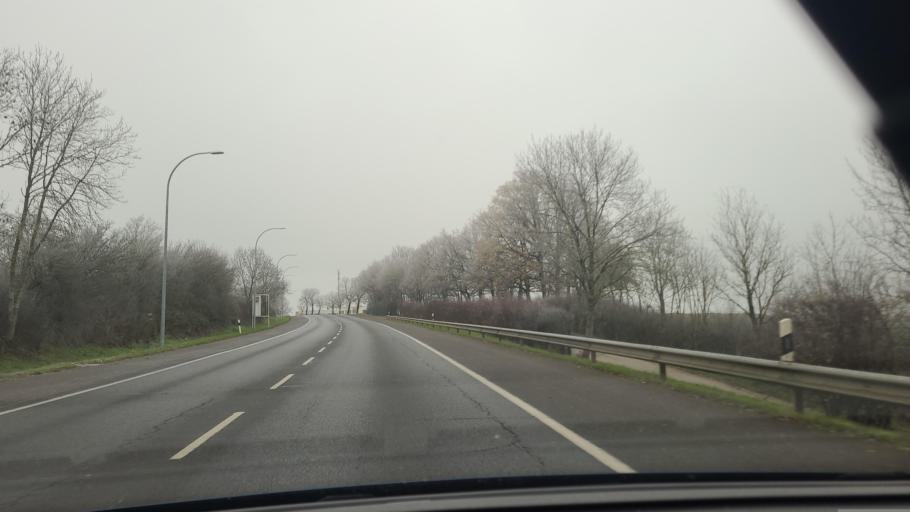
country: LU
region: Luxembourg
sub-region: Canton de Capellen
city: Garnich
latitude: 49.6404
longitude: 5.9556
